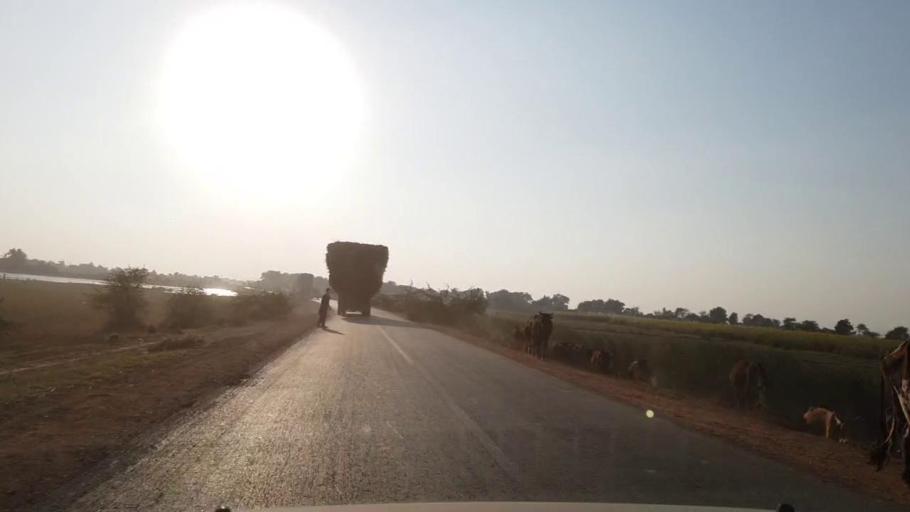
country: PK
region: Sindh
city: Mirpur Batoro
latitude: 24.6945
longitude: 68.1908
